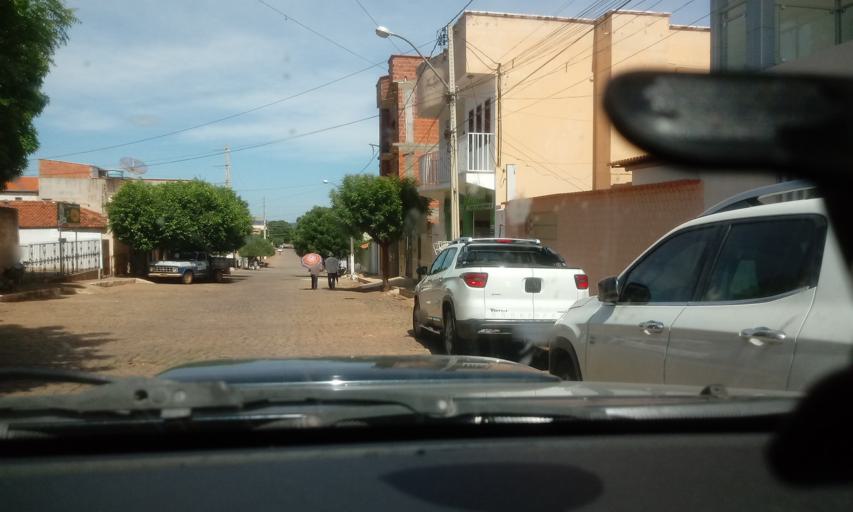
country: BR
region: Bahia
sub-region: Riacho De Santana
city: Riacho de Santana
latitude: -13.6107
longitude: -42.9352
